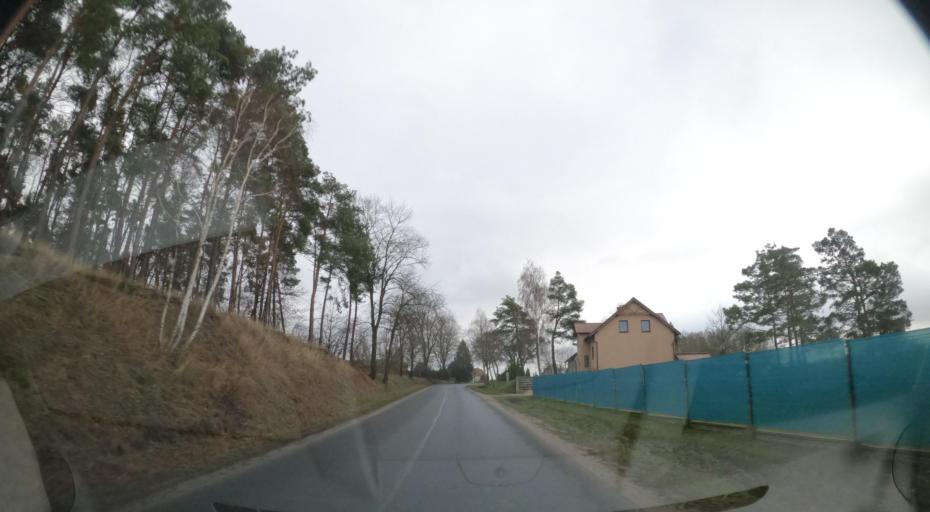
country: PL
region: Greater Poland Voivodeship
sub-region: Powiat pilski
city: Lobzenica
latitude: 53.2478
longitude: 17.2845
